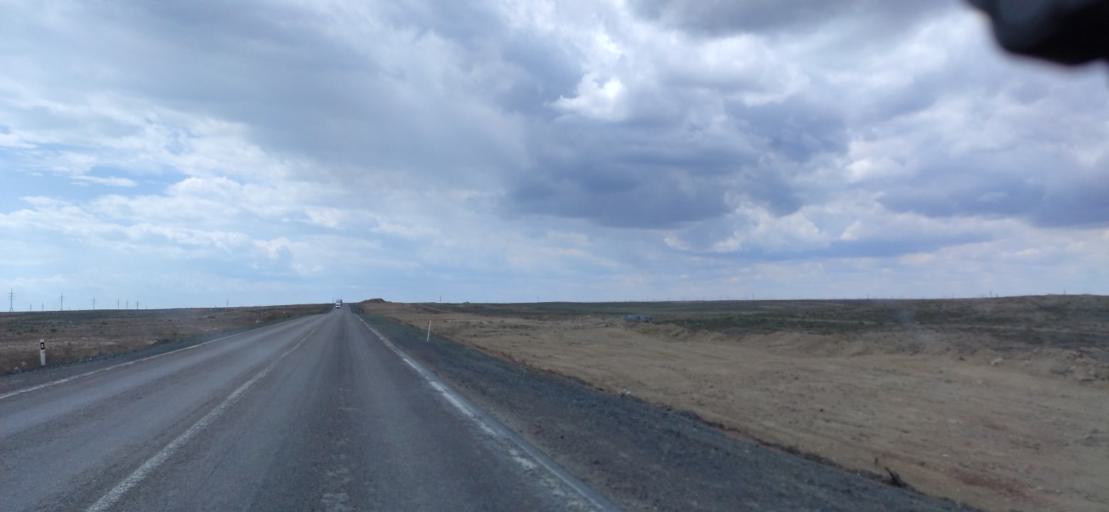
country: KZ
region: Qaraghandy
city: Saryshaghan
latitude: 46.0800
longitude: 73.6043
